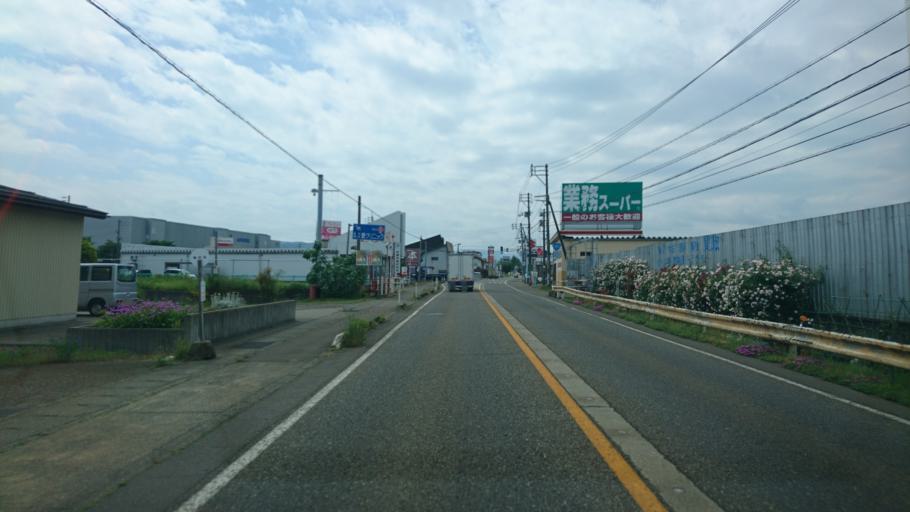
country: JP
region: Niigata
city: Arai
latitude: 37.0569
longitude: 138.2602
